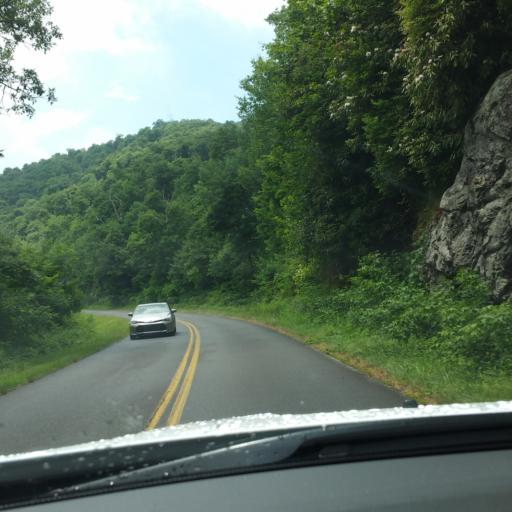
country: US
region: North Carolina
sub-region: Transylvania County
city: Brevard
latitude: 35.3648
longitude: -82.7950
